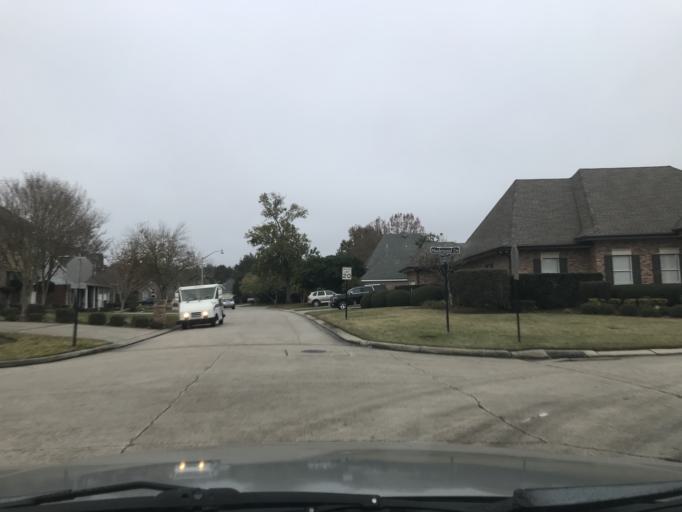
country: US
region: Louisiana
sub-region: Jefferson Parish
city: Woodmere
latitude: 29.8711
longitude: -90.0920
